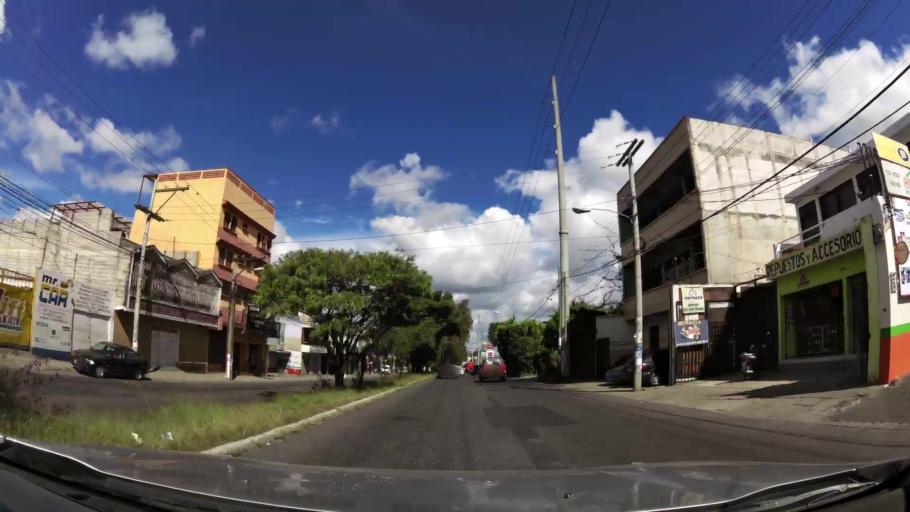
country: GT
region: Guatemala
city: Mixco
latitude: 14.6584
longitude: -90.5670
